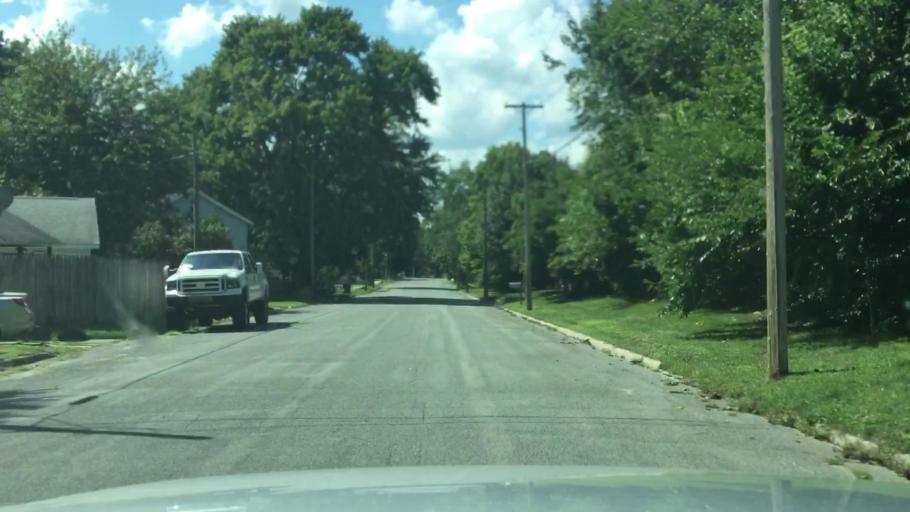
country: US
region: Michigan
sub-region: Lenawee County
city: Clinton
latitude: 42.0741
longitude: -83.9684
